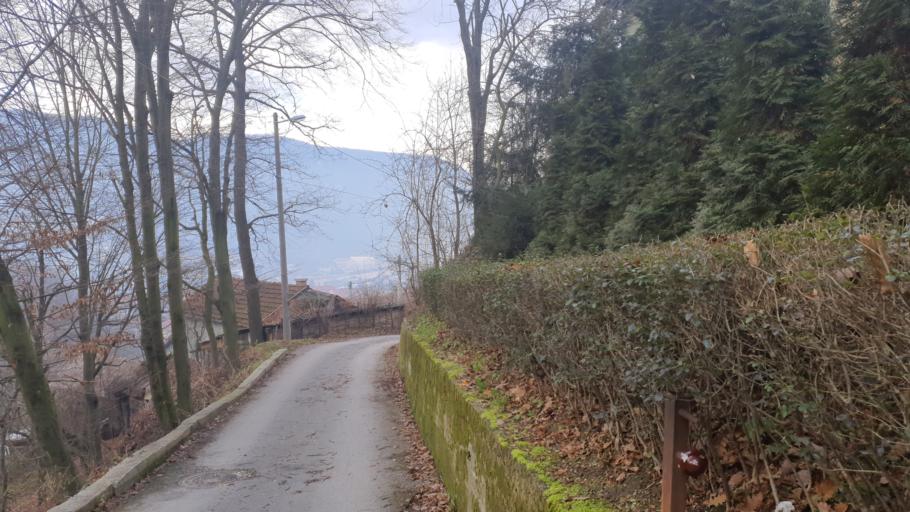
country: RS
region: Central Serbia
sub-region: Zlatiborski Okrug
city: Uzice
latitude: 43.8490
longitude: 19.8685
